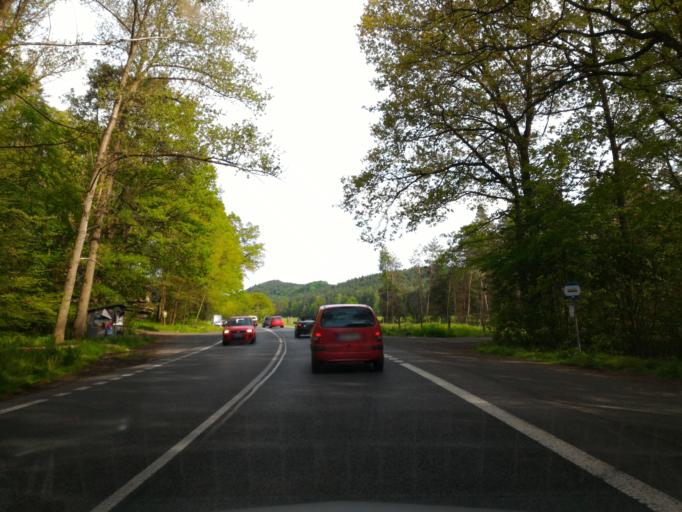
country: CZ
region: Liberecky
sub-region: Okres Ceska Lipa
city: Ceska Lipa
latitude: 50.6195
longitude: 14.5410
